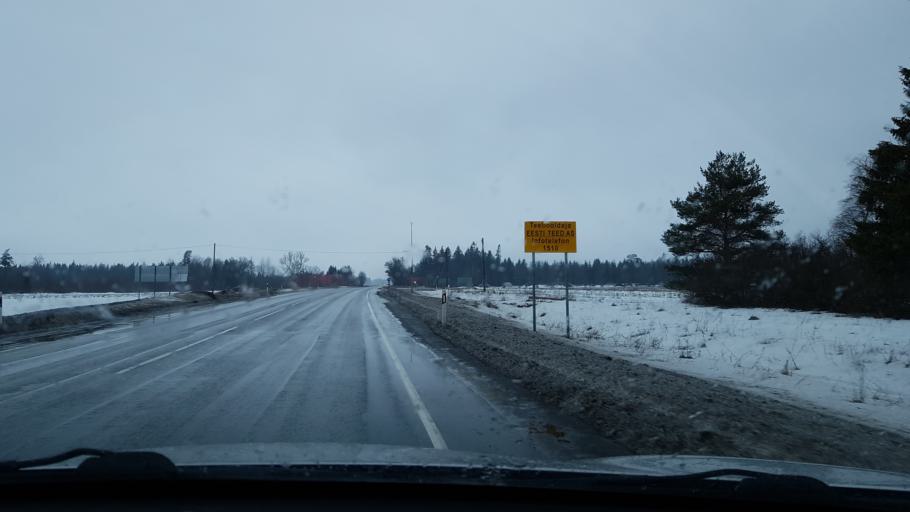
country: EE
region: Raplamaa
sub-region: Kohila vald
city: Kohila
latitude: 59.1989
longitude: 24.7843
